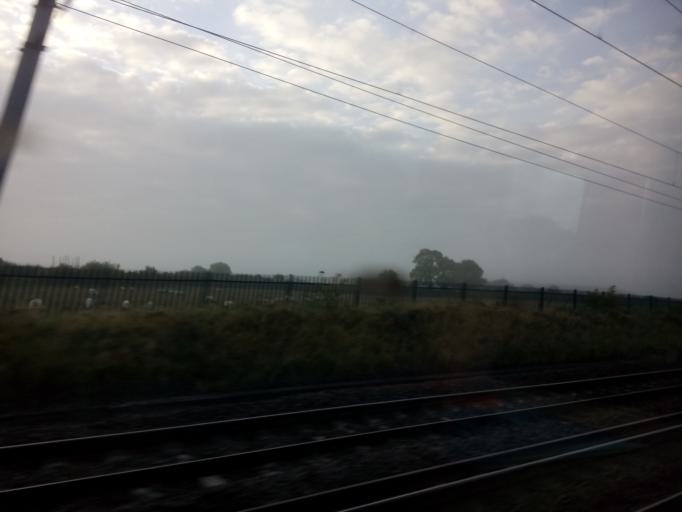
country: GB
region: England
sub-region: City of York
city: Copmanthorpe
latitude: 53.9065
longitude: -1.1458
